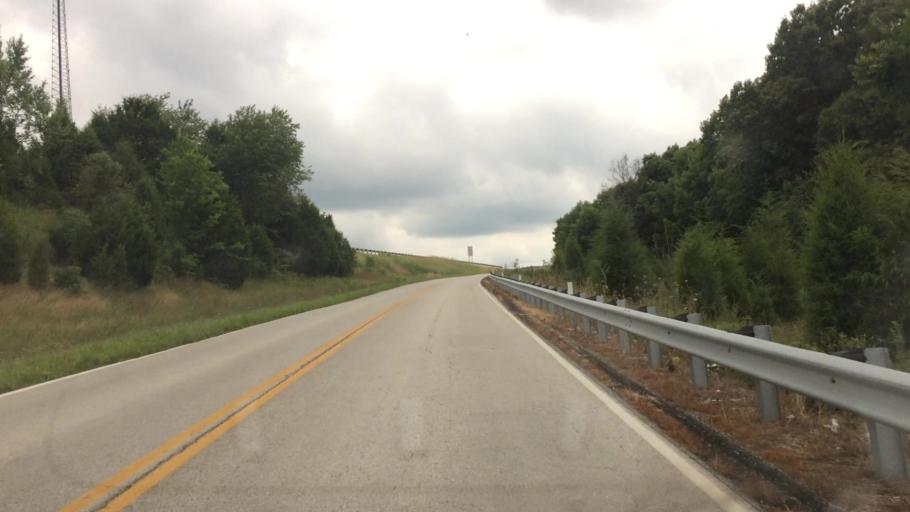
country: US
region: Missouri
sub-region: Webster County
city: Marshfield
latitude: 37.3019
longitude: -93.0089
